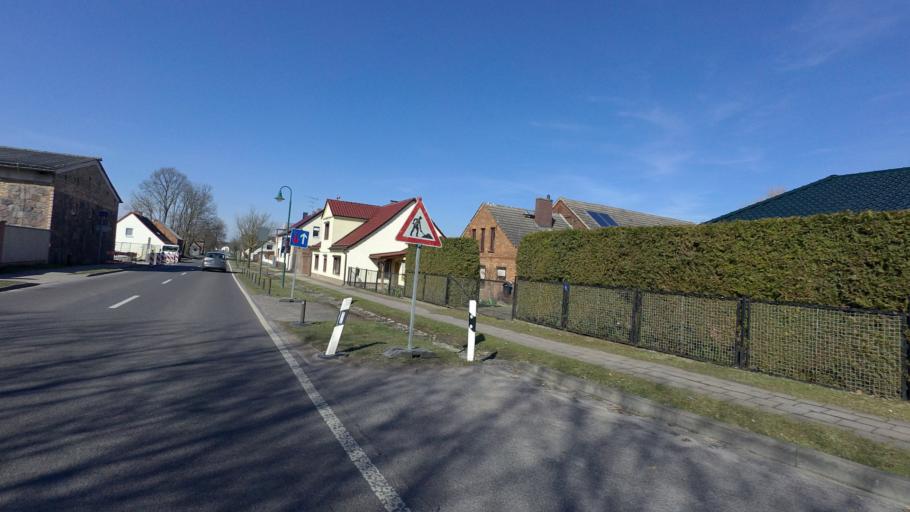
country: DE
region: Brandenburg
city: Eberswalde
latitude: 52.7739
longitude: 13.8373
